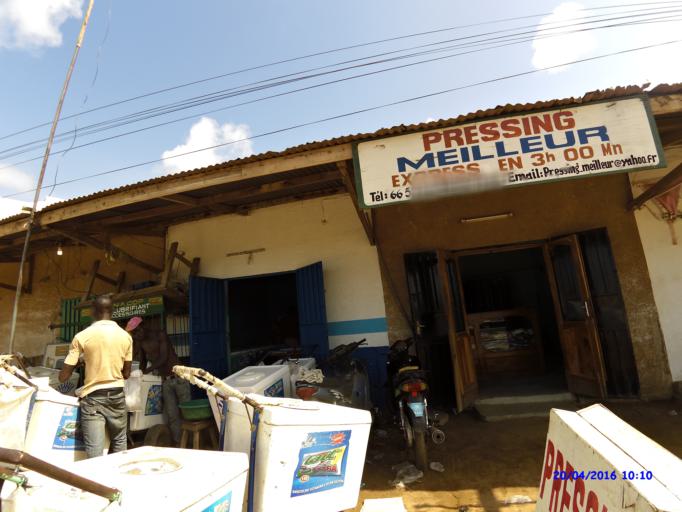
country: BJ
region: Atlantique
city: Hevie
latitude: 6.3878
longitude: 2.2975
